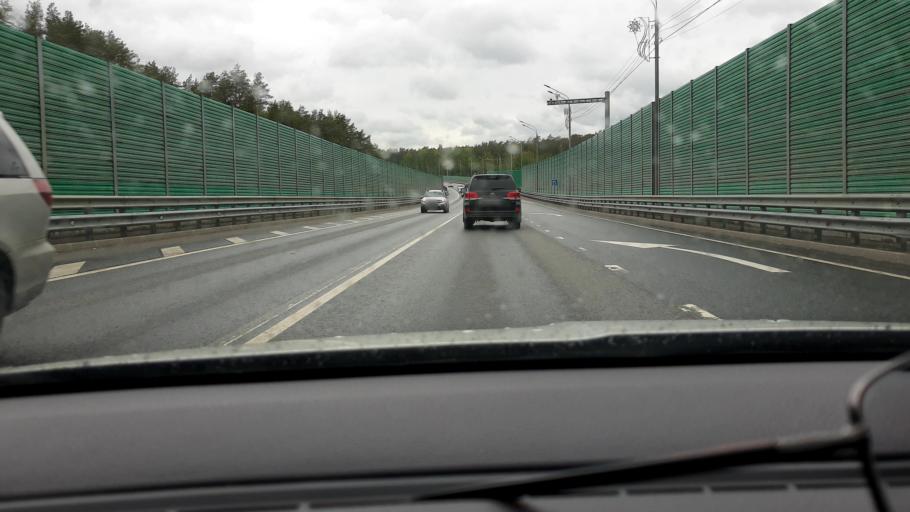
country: RU
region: Moskovskaya
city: Petrovo-Dal'neye
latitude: 55.7272
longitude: 37.2002
